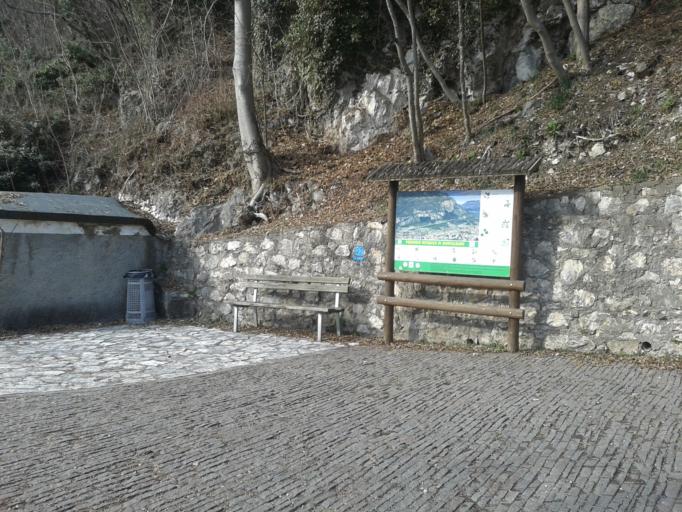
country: IT
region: Trentino-Alto Adige
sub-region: Provincia di Trento
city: Mori
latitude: 45.8557
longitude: 10.9791
